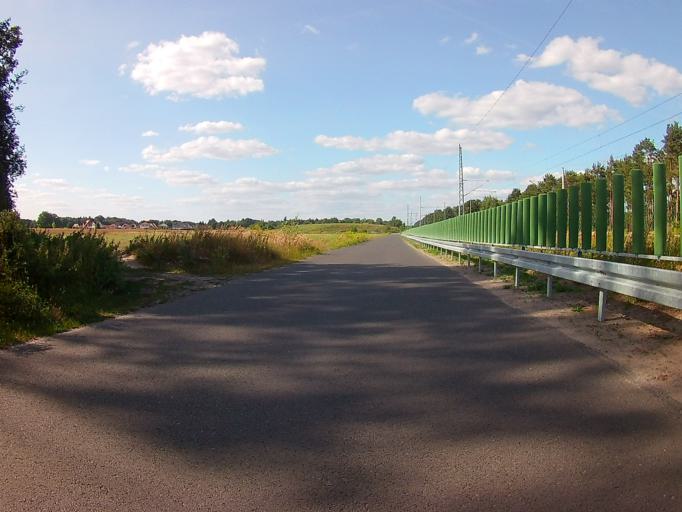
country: DE
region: Brandenburg
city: Zeuthen
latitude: 52.3576
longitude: 13.6214
